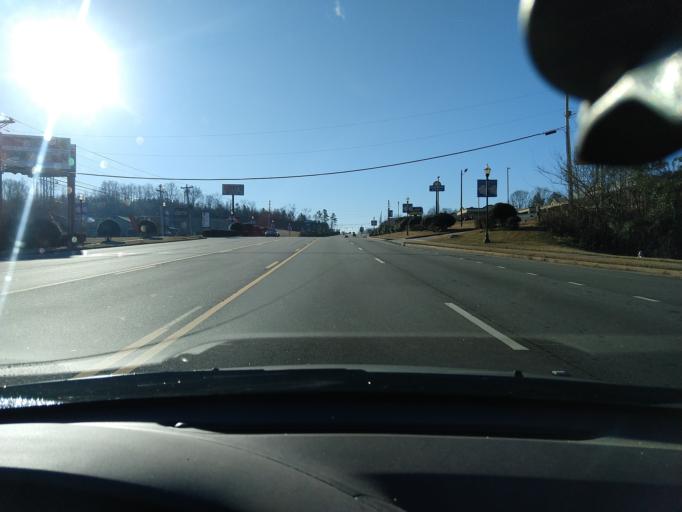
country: US
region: Georgia
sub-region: Jackson County
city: Commerce
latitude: 34.2493
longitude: -83.4603
